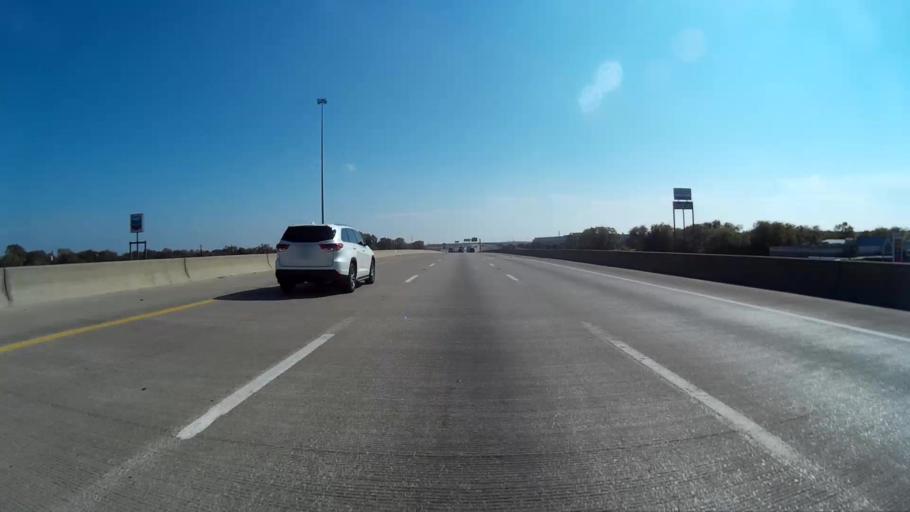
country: US
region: Texas
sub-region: Dallas County
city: Wilmer
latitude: 32.5913
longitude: -96.6793
